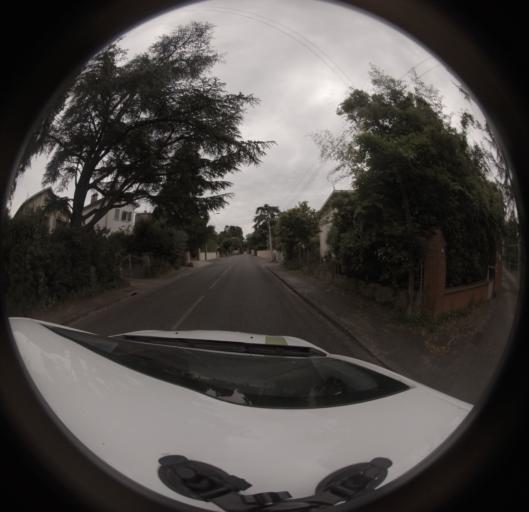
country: FR
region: Midi-Pyrenees
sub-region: Departement du Tarn-et-Garonne
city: Montauban
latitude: 44.0043
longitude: 1.3743
